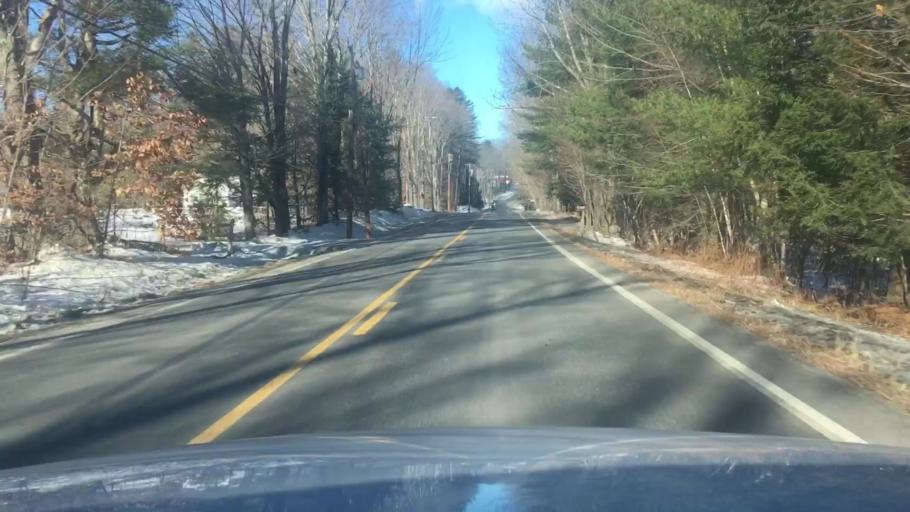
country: US
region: Maine
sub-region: Somerset County
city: Skowhegan
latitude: 44.7289
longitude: -69.6783
